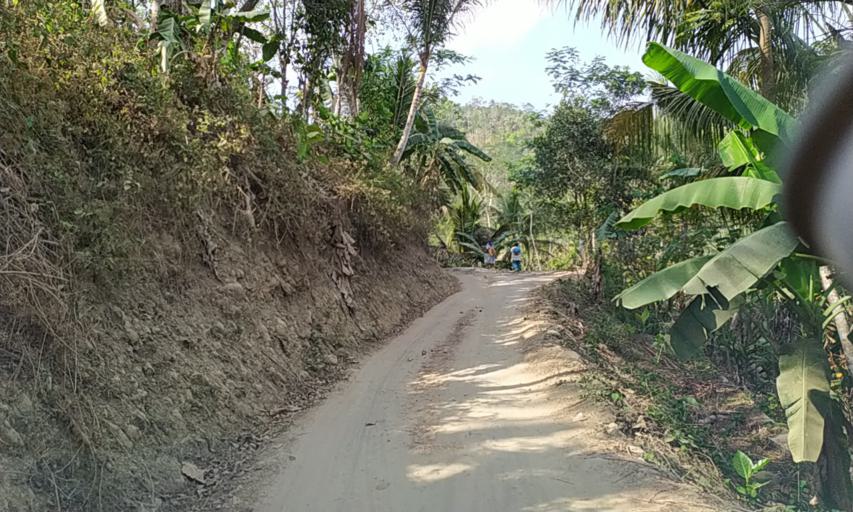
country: ID
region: Central Java
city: Jambuluwuk
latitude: -7.3189
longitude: 108.9073
